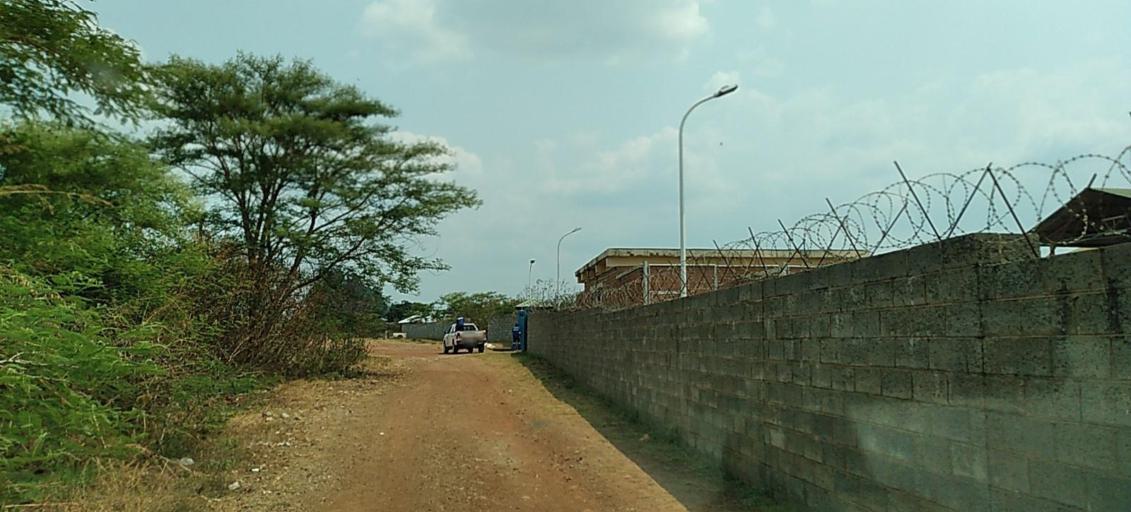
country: ZM
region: Copperbelt
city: Kalulushi
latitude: -12.8235
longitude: 28.0763
